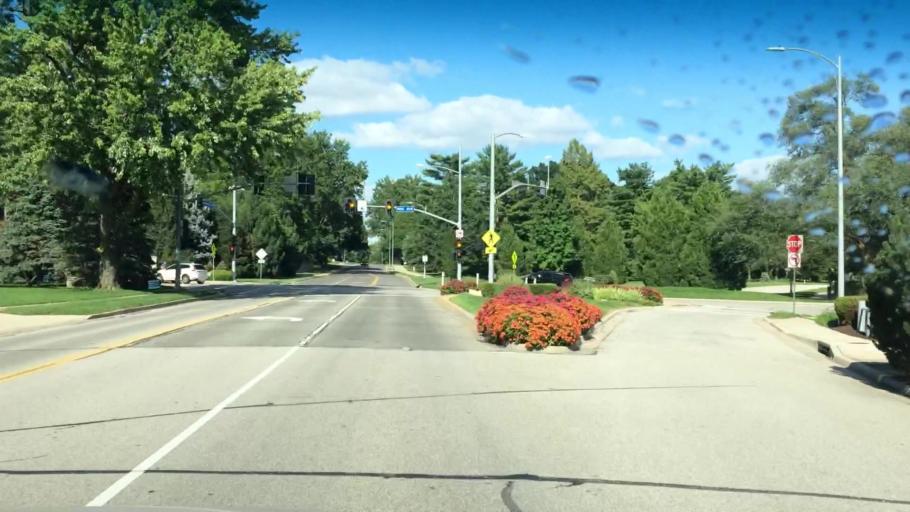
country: US
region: Kansas
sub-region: Johnson County
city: Prairie Village
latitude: 38.9726
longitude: -94.6382
